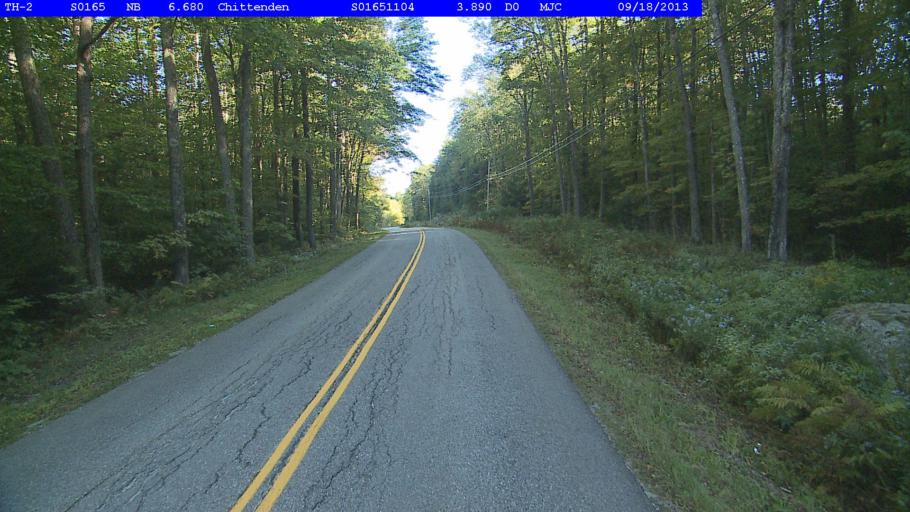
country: US
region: Vermont
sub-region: Rutland County
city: Rutland
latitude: 43.7301
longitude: -72.9708
